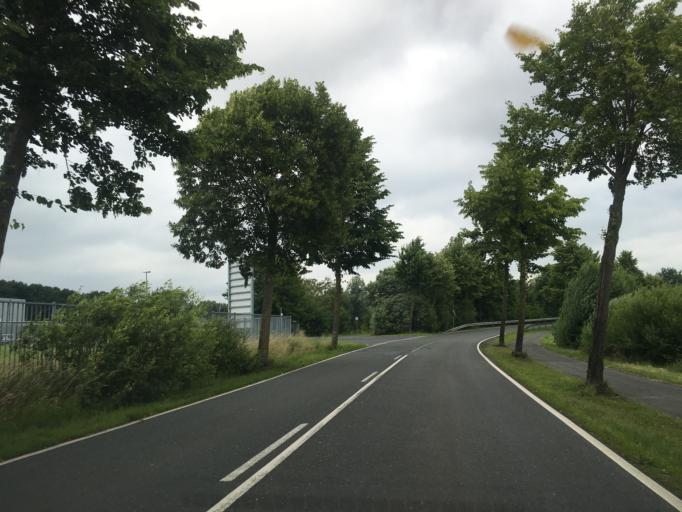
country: DE
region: North Rhine-Westphalia
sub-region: Regierungsbezirk Munster
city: Steinfurt
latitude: 52.1540
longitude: 7.3126
